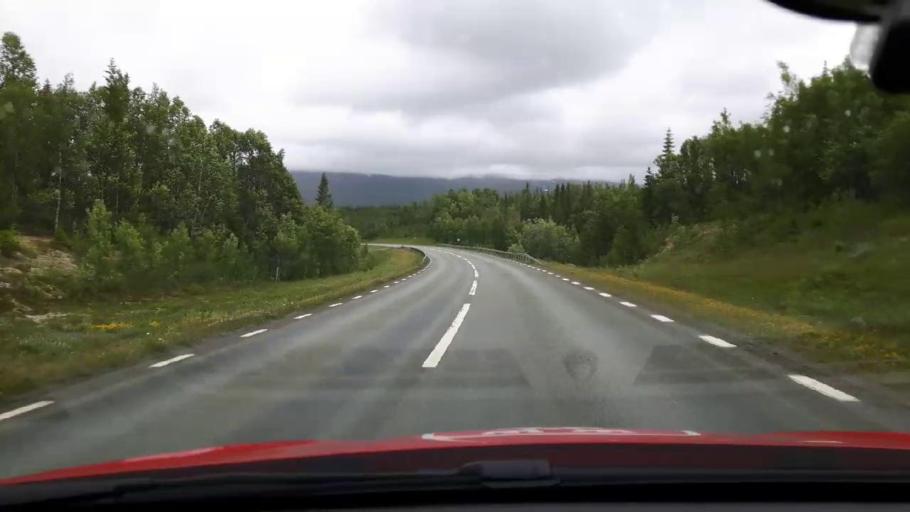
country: NO
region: Nord-Trondelag
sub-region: Meraker
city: Meraker
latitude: 63.2579
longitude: 12.1774
